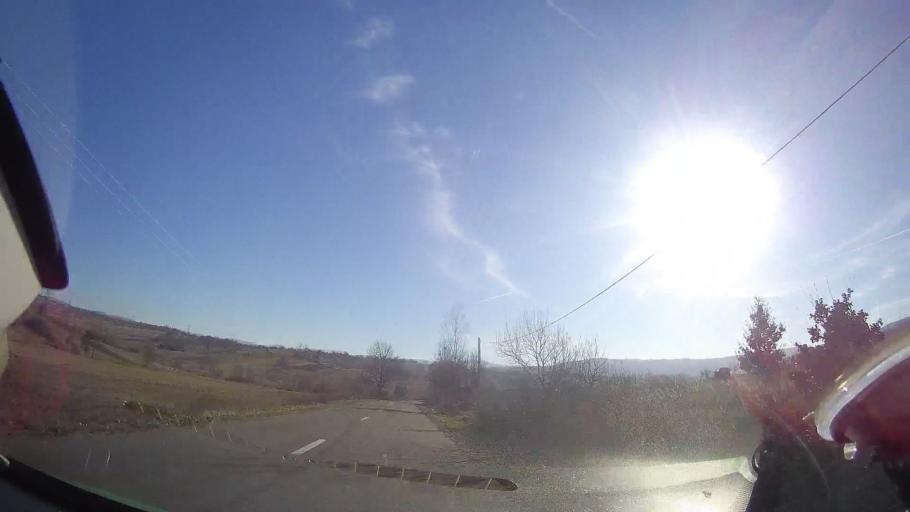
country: RO
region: Bihor
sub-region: Comuna Suncuius
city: Balnaca
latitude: 46.9661
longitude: 22.5512
